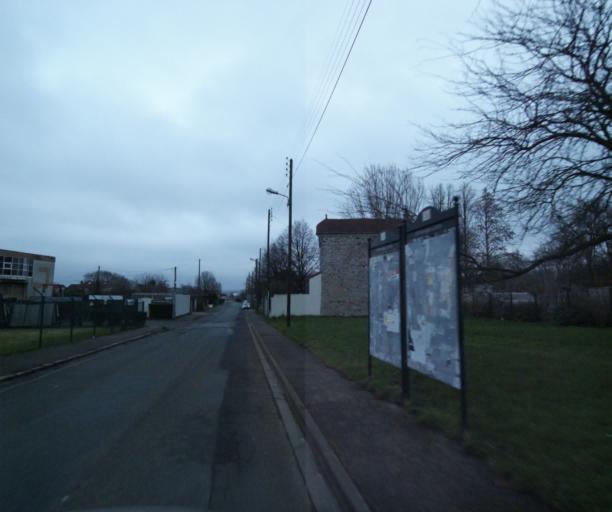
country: FR
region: Ile-de-France
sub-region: Departement du Val-de-Marne
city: Villeneuve-le-Roi
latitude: 48.7296
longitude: 2.4117
